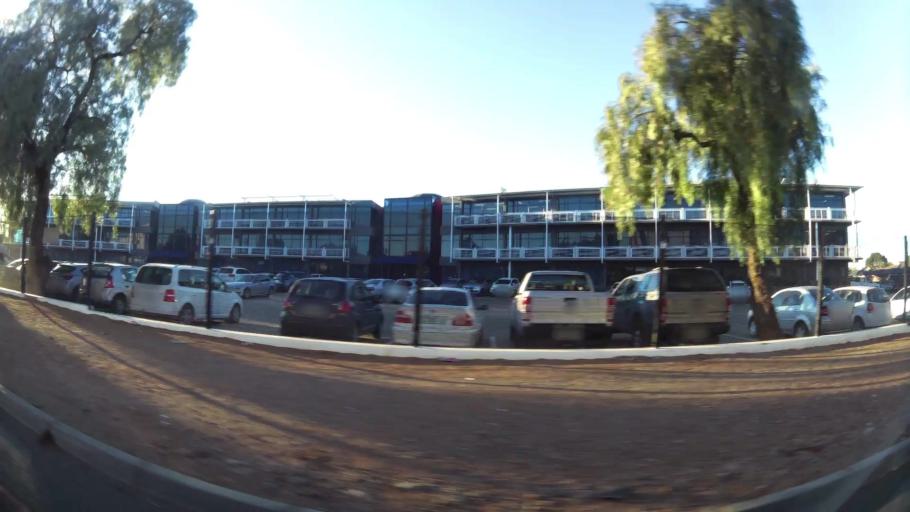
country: ZA
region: Northern Cape
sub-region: Frances Baard District Municipality
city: Kimberley
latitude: -28.7611
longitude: 24.7597
